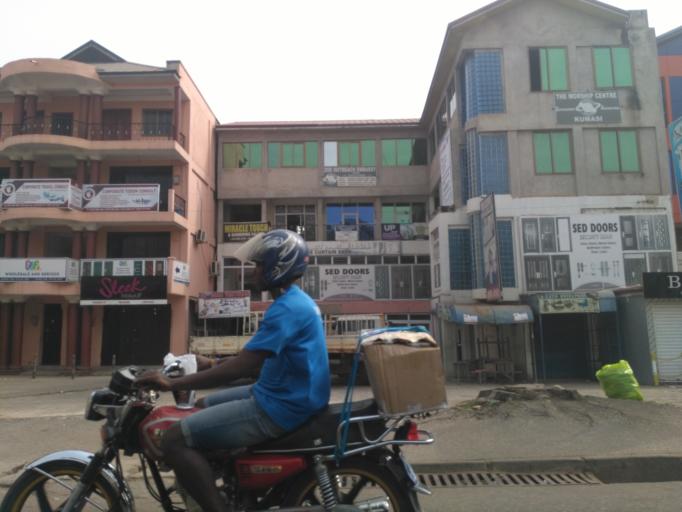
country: GH
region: Ashanti
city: Kumasi
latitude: 6.6899
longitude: -1.6194
